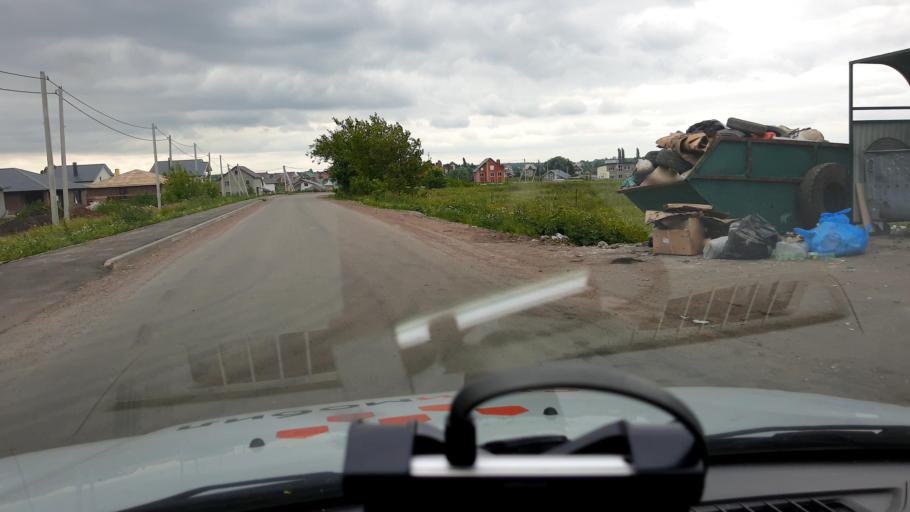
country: RU
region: Bashkortostan
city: Kabakovo
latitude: 54.6520
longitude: 56.1912
